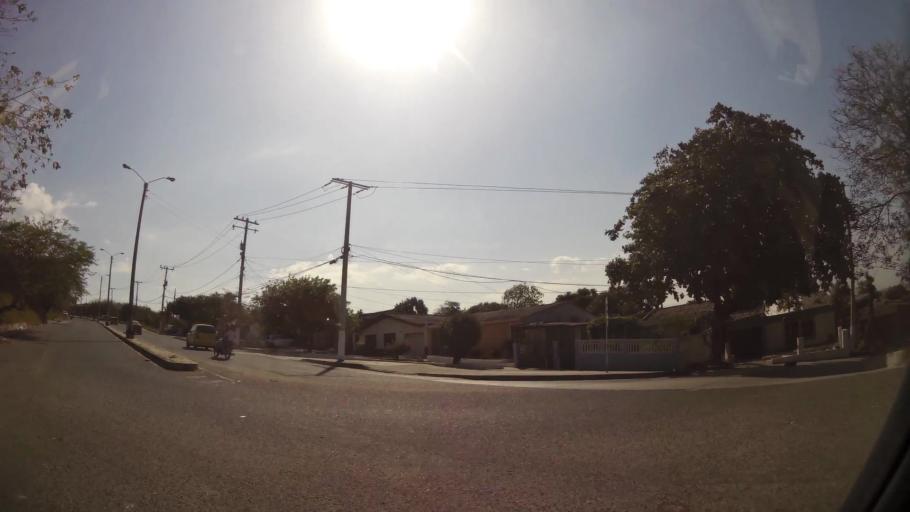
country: CO
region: Atlantico
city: Barranquilla
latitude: 10.9849
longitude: -74.8246
